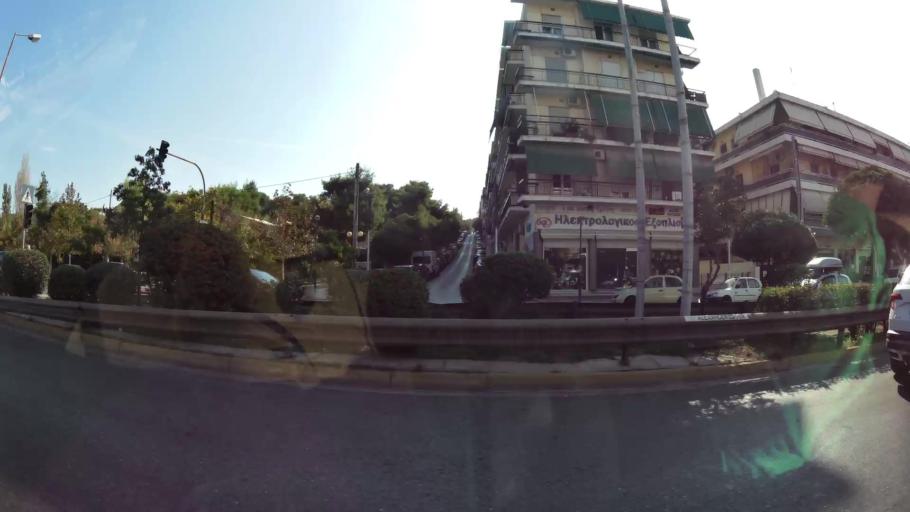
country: GR
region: Attica
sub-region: Nomarchia Athinas
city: Galatsi
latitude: 38.0203
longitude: 23.7568
